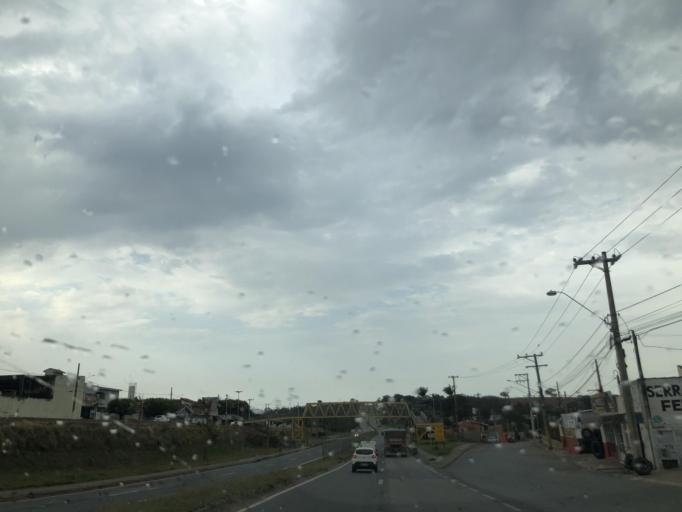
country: BR
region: Sao Paulo
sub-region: Salto De Pirapora
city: Salto de Pirapora
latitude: -23.6397
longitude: -47.5748
